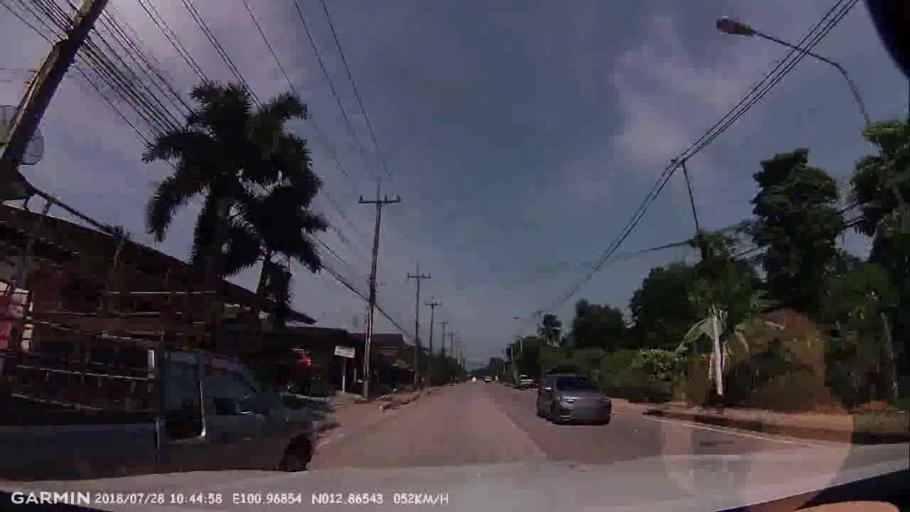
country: TH
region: Chon Buri
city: Phatthaya
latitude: 12.8654
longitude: 100.9684
